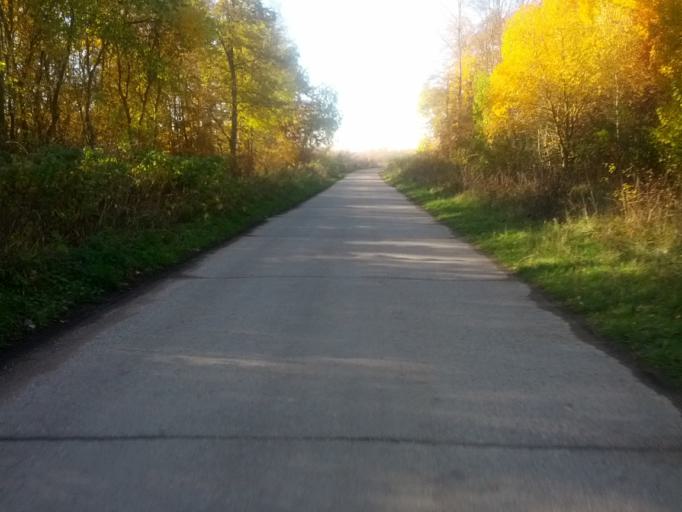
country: DE
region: Thuringia
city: Remstadt
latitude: 50.9582
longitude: 10.6508
